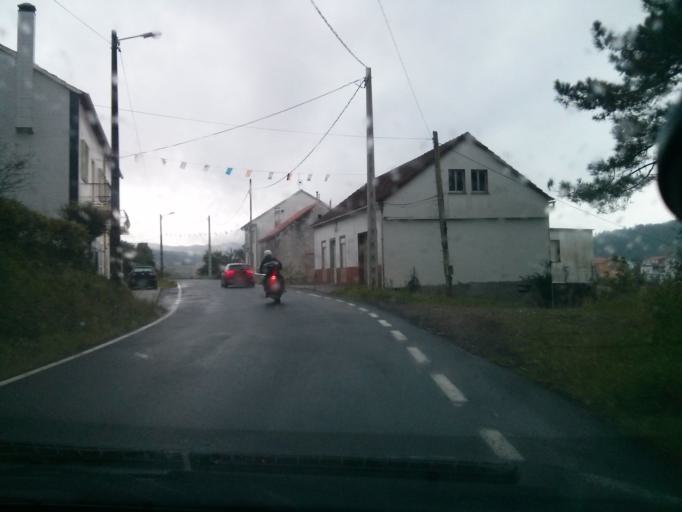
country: ES
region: Galicia
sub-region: Provincia da Coruna
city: Outes
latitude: 42.8332
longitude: -8.8730
